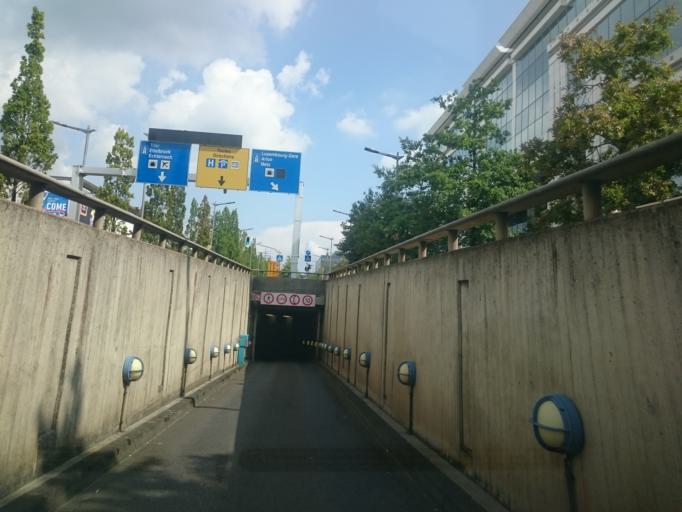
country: LU
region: Luxembourg
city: Kirchberg
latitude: 49.6322
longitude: 6.1715
